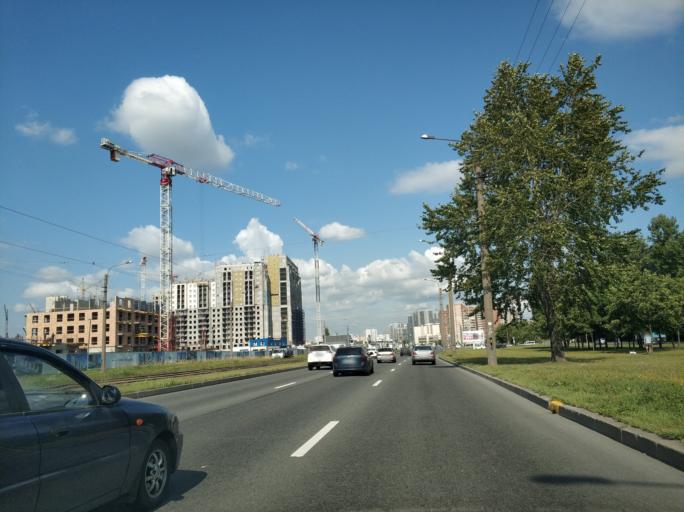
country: RU
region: St.-Petersburg
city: Obukhovo
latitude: 59.8985
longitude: 30.4602
